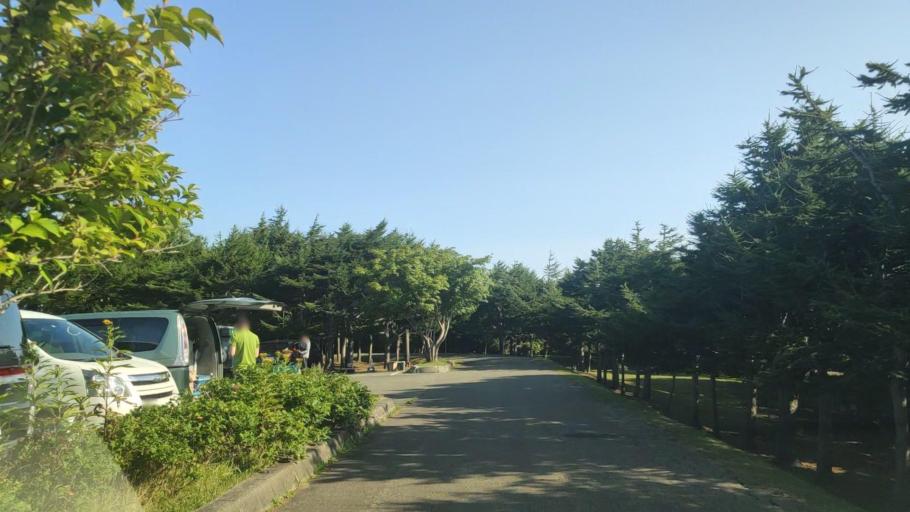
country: JP
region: Hokkaido
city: Wakkanai
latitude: 45.4121
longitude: 141.6707
